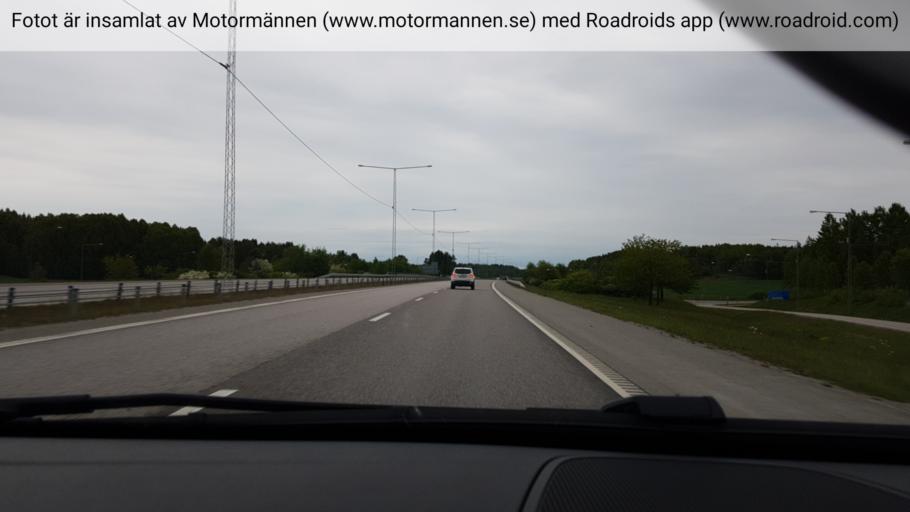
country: SE
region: Stockholm
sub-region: Haninge Kommun
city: Jordbro
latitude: 59.1203
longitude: 18.1310
